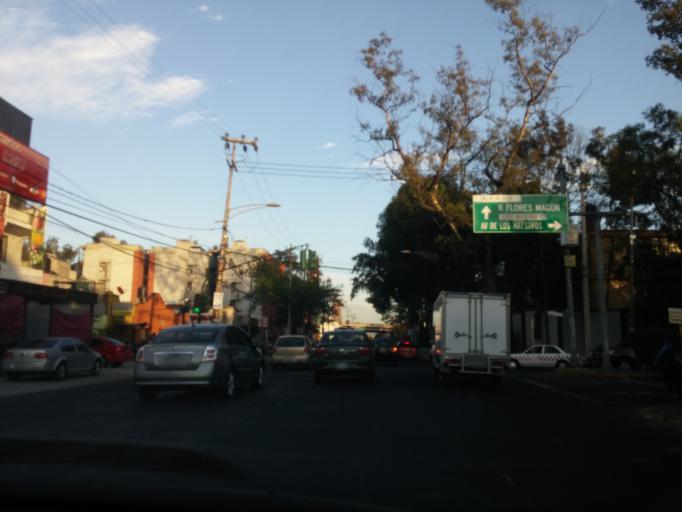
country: MX
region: Mexico City
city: Cuauhtemoc
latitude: 19.4562
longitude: -99.1662
